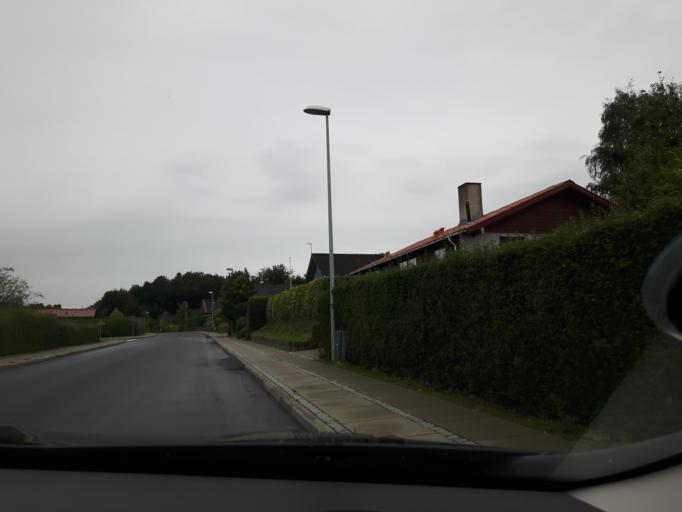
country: DK
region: Central Jutland
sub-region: Skanderborg Kommune
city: Ry
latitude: 56.1534
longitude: 9.8027
